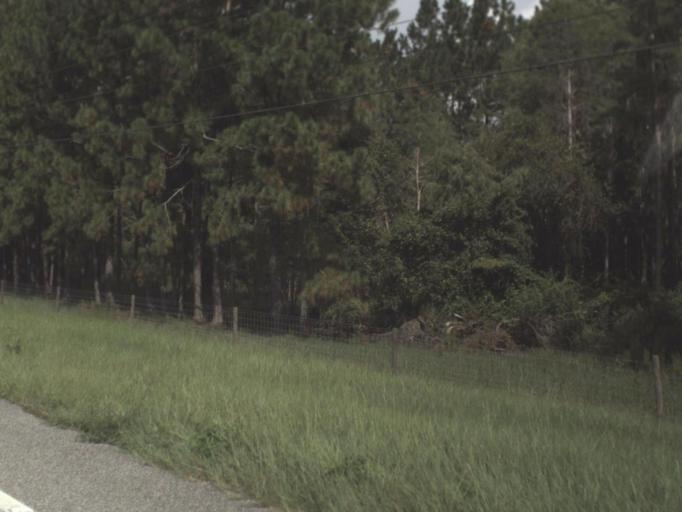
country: US
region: Florida
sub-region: Pasco County
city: Land O' Lakes
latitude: 28.3224
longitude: -82.4303
